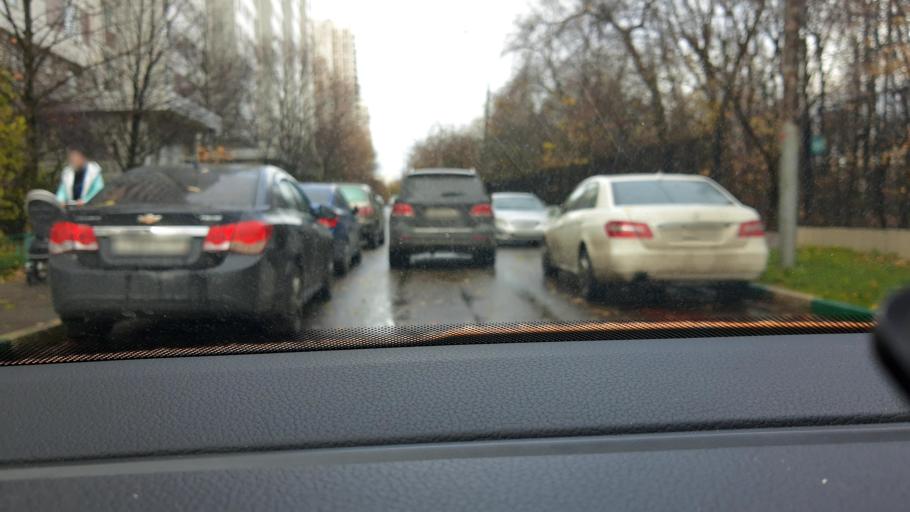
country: RU
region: Moskovskaya
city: Bol'shaya Setun'
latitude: 55.7397
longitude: 37.4393
